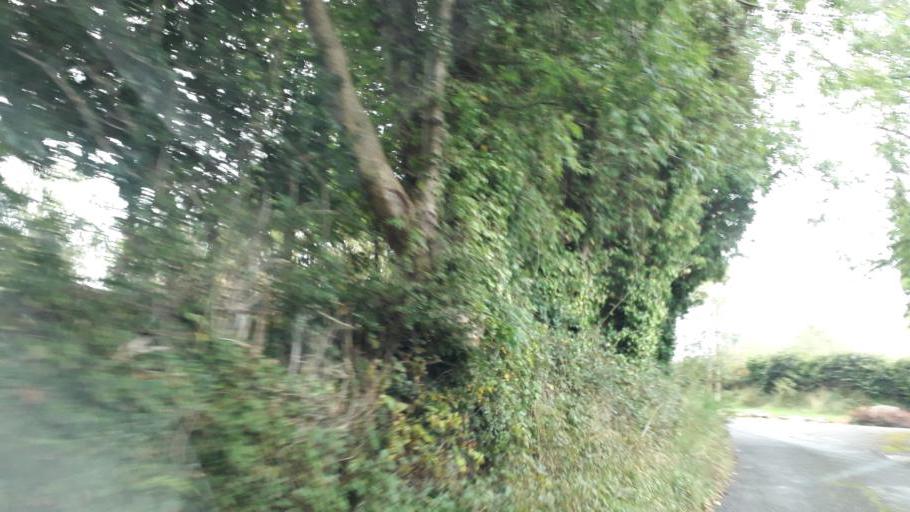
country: IE
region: Leinster
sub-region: Wicklow
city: Enniskerry
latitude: 53.1676
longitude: -6.1984
